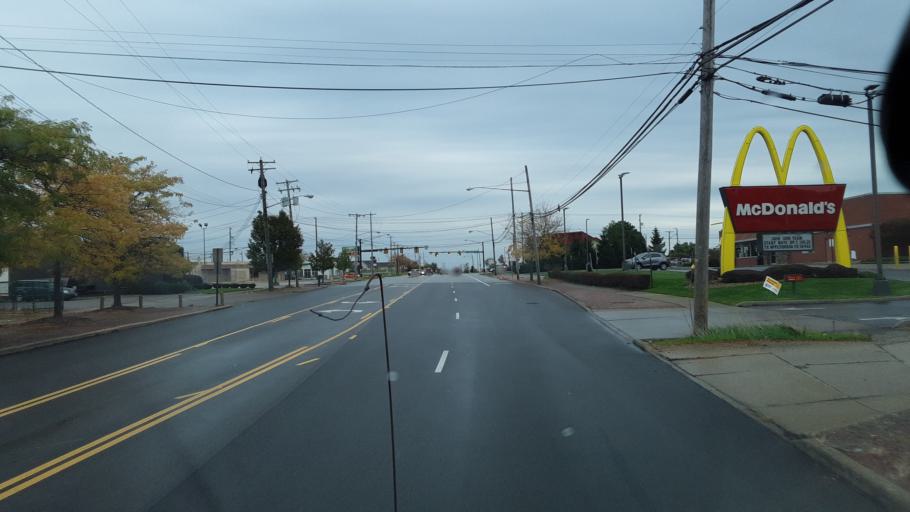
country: US
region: Ohio
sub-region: Summit County
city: Portage Lakes
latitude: 41.0296
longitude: -81.4939
